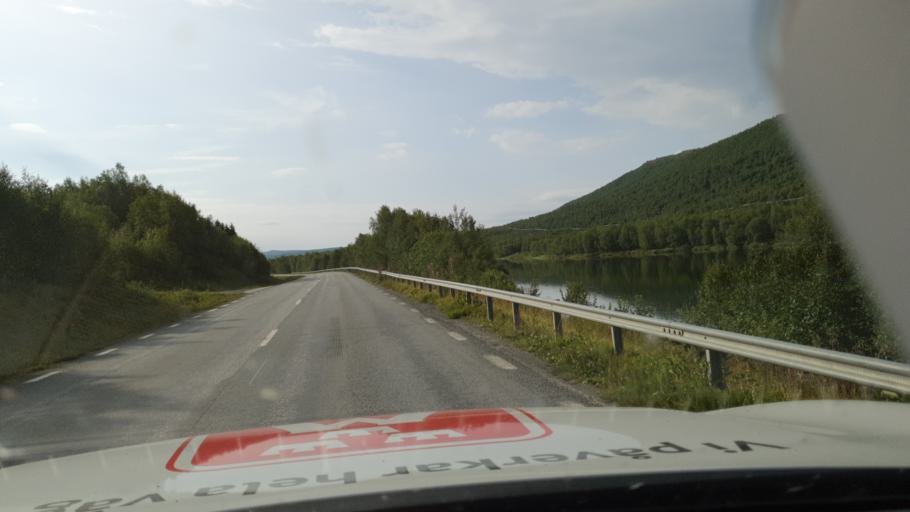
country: NO
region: Nordland
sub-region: Rana
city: Mo i Rana
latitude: 65.7890
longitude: 15.1047
